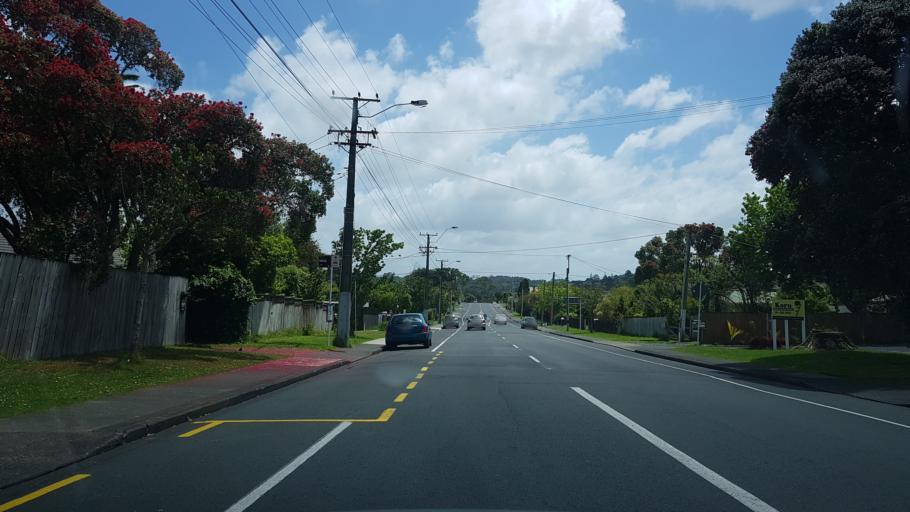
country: NZ
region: Auckland
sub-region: Auckland
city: North Shore
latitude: -36.7948
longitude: 174.7008
